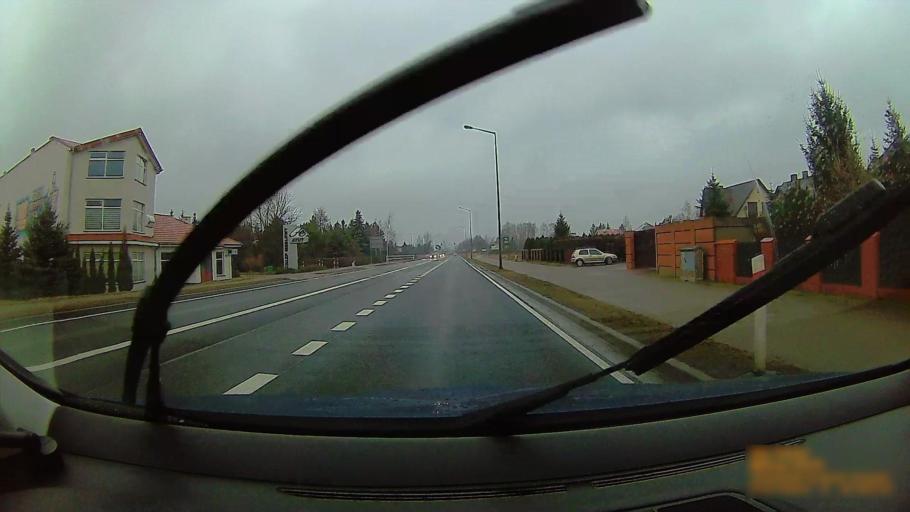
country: PL
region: Greater Poland Voivodeship
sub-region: Konin
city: Konin
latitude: 52.1805
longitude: 18.2700
